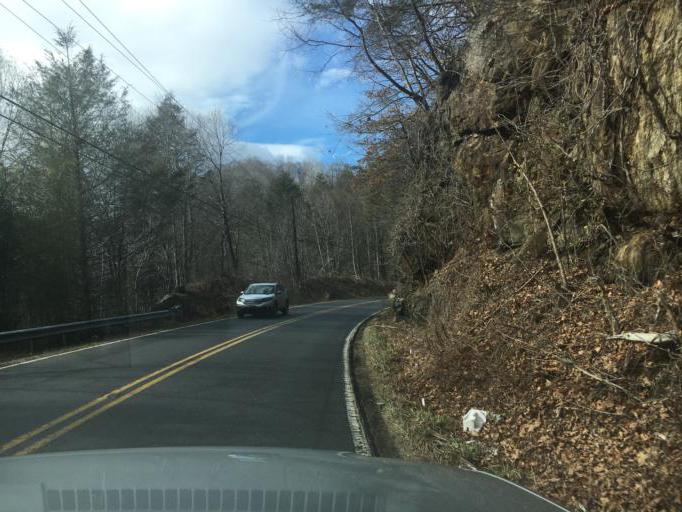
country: US
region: North Carolina
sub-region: Haywood County
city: Canton
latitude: 35.4456
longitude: -82.8181
